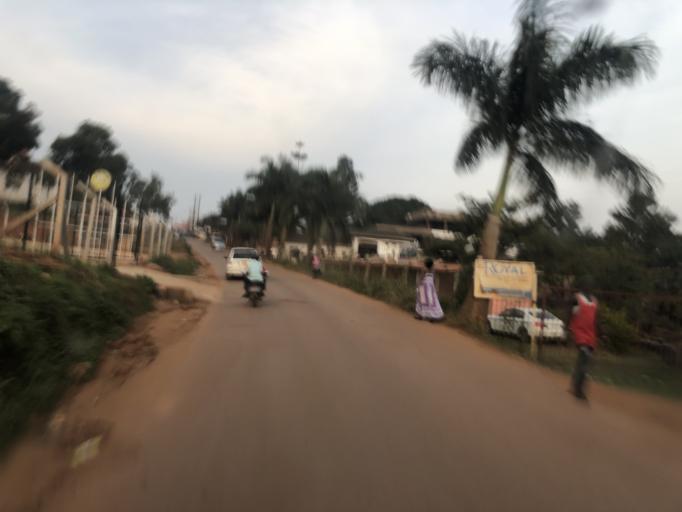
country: UG
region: Central Region
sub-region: Kampala District
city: Kampala
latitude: 0.2722
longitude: 32.5503
